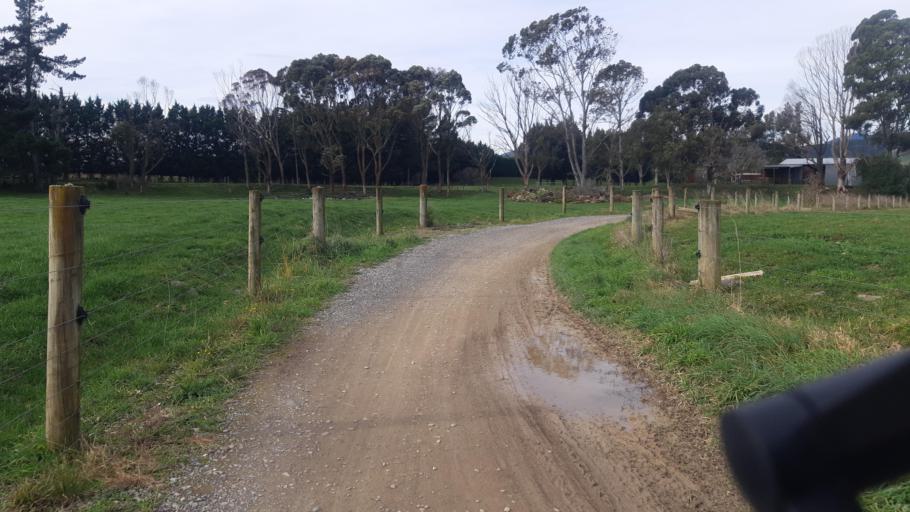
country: NZ
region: Tasman
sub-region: Tasman District
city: Brightwater
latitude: -41.3564
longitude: 173.1176
